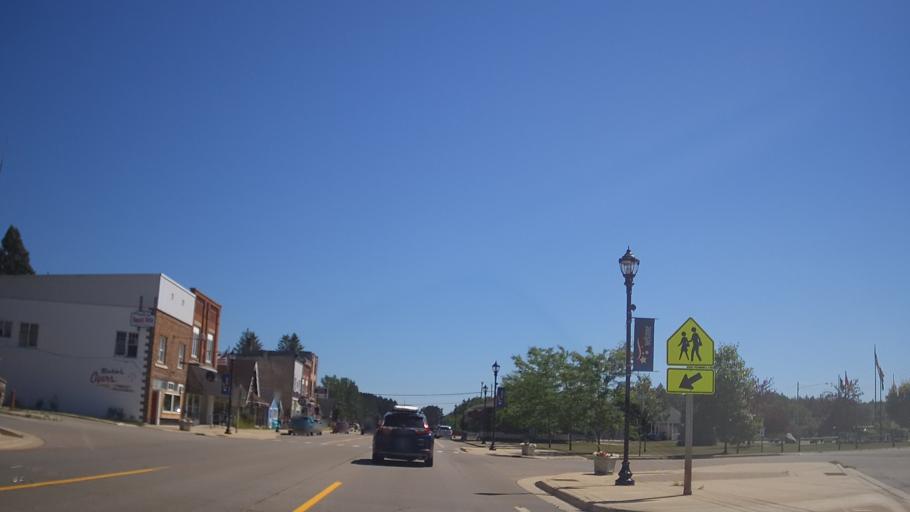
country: US
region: Michigan
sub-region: Cheboygan County
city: Indian River
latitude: 45.5537
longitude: -84.7844
